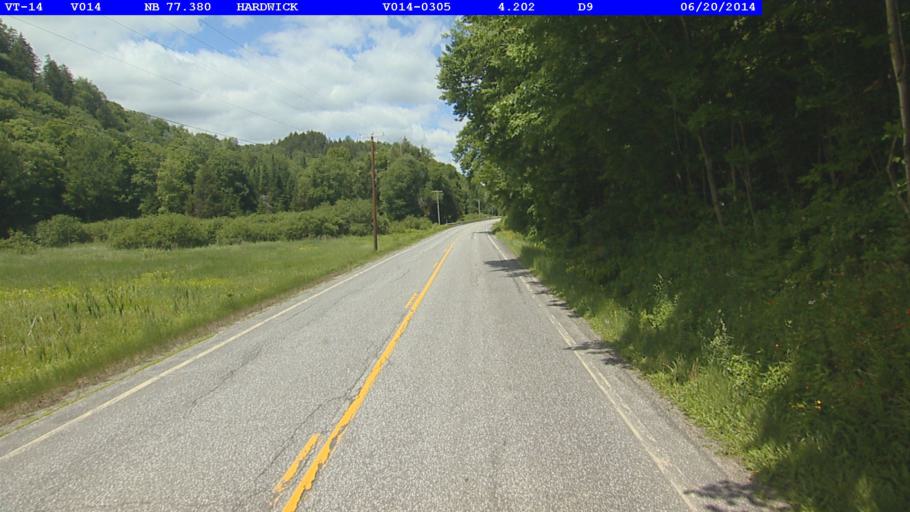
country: US
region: Vermont
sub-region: Caledonia County
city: Hardwick
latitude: 44.5541
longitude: -72.3693
